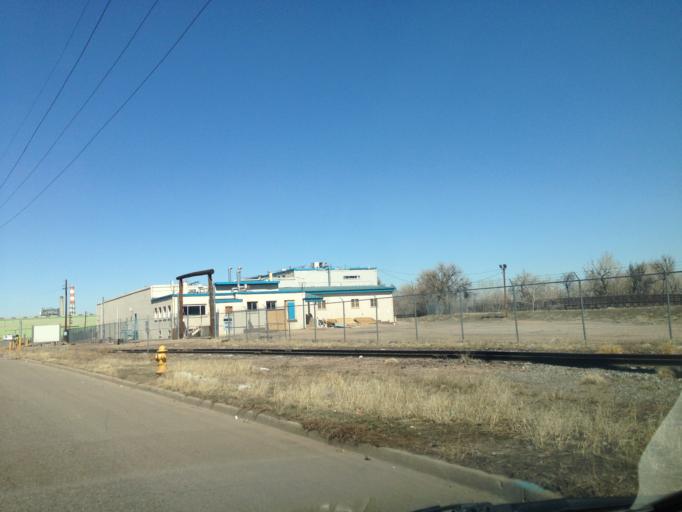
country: US
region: Colorado
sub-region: Adams County
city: Commerce City
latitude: 39.7918
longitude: -104.9688
